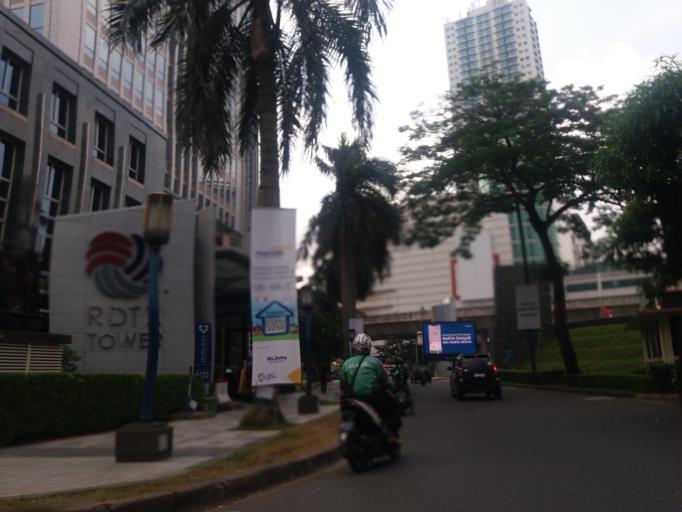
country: ID
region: Jakarta Raya
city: Jakarta
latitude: -6.2254
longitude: 106.8258
